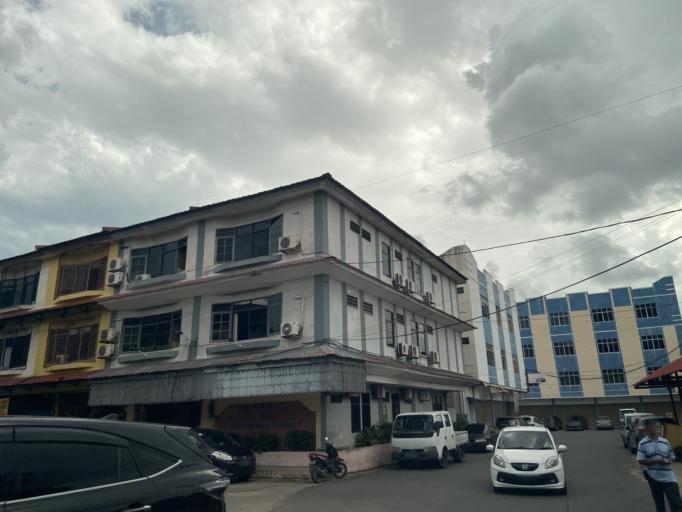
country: SG
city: Singapore
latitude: 1.1358
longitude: 104.0099
